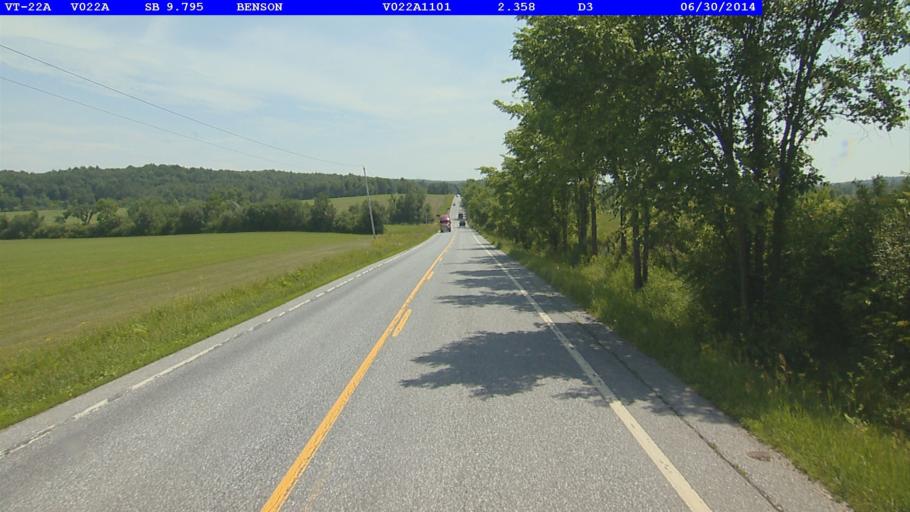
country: US
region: Vermont
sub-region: Rutland County
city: Fair Haven
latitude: 43.7024
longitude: -73.2955
